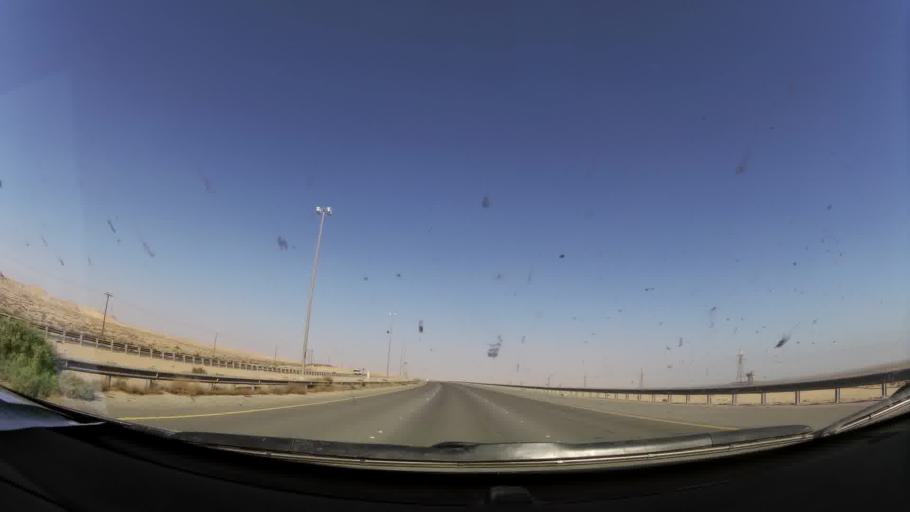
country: KW
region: Muhafazat al Jahra'
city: Al Jahra'
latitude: 29.4956
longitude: 47.7910
